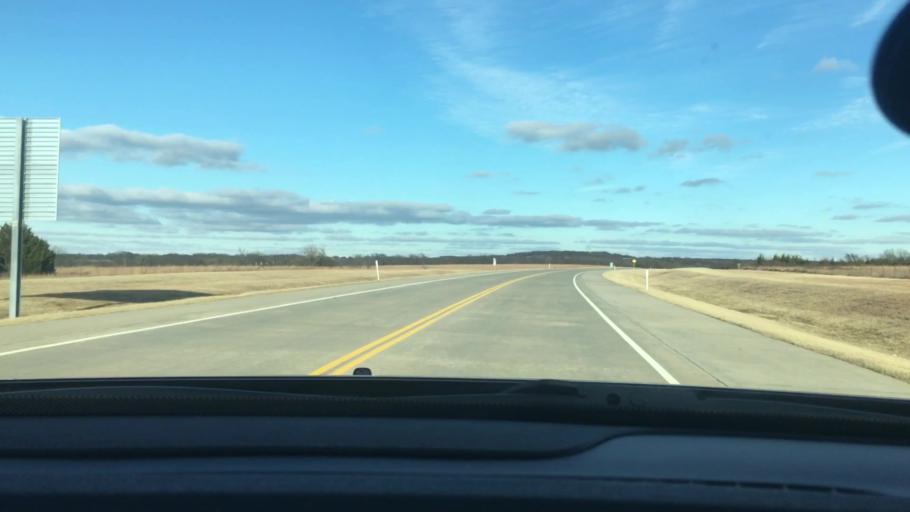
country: US
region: Oklahoma
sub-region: Murray County
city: Sulphur
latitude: 34.5815
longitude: -96.9206
